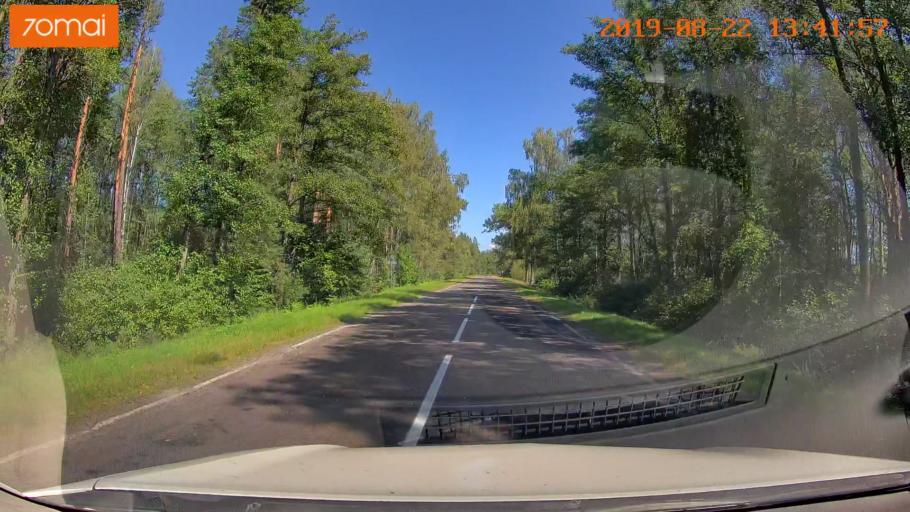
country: BY
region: Mogilev
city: Asipovichy
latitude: 53.2395
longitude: 28.4075
